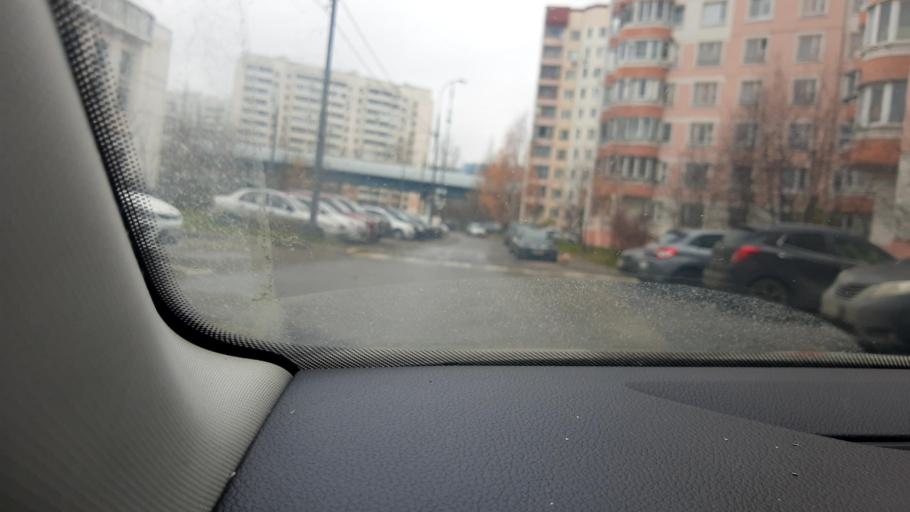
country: RU
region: Moscow
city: Annino
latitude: 55.5495
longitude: 37.5643
